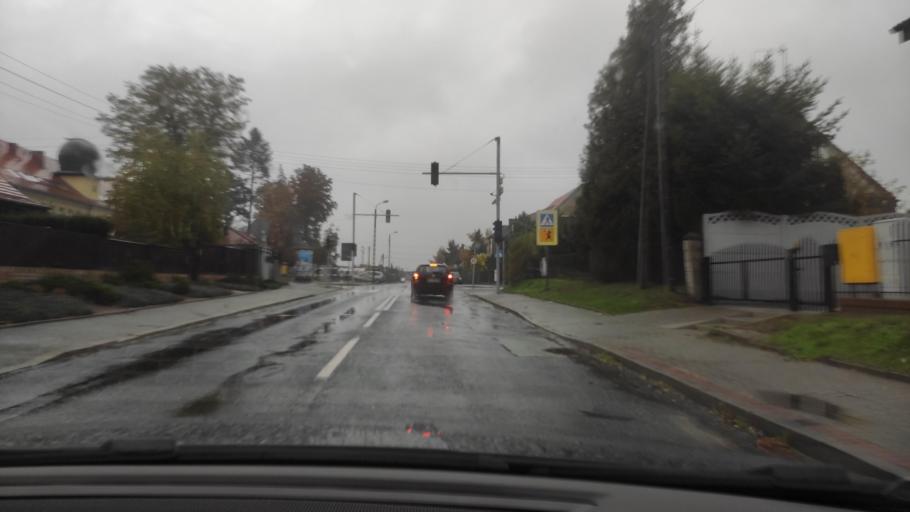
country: PL
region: Greater Poland Voivodeship
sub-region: Powiat poznanski
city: Kornik
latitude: 52.2515
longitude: 17.0898
